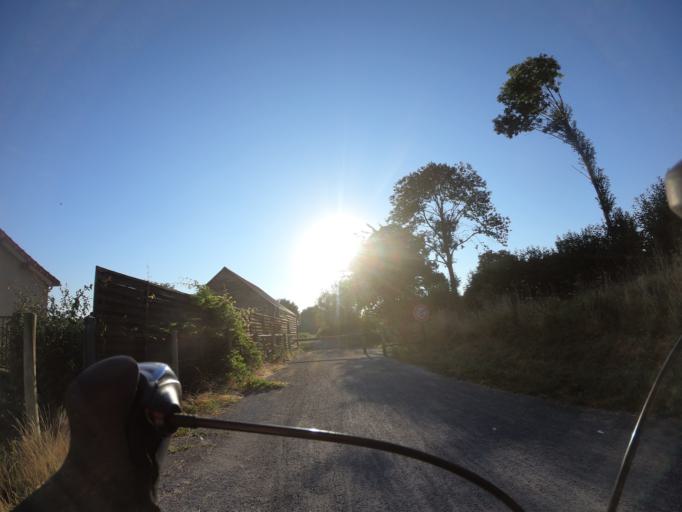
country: FR
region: Lower Normandy
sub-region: Departement de la Manche
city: Isigny-le-Buat
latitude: 48.6367
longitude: -1.2023
